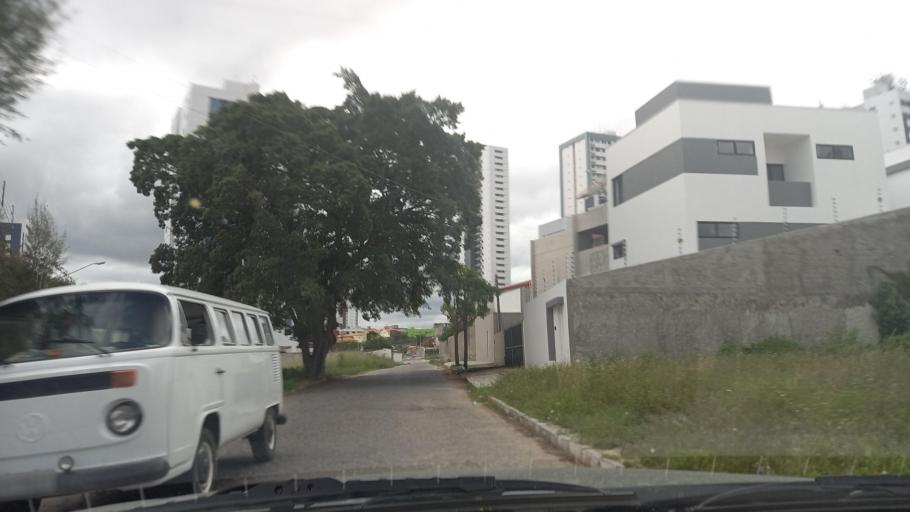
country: BR
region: Pernambuco
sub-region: Caruaru
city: Caruaru
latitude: -8.2682
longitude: -35.9677
